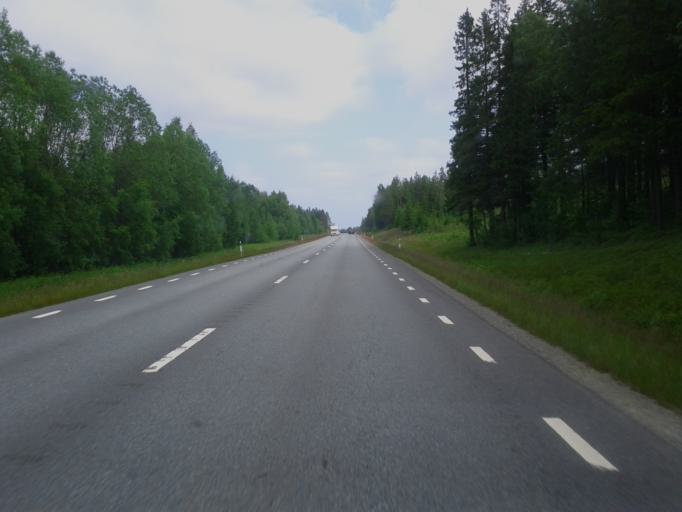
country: SE
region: Vaesterbotten
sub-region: Skelleftea Kommun
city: Burea
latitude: 64.3402
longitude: 21.2776
